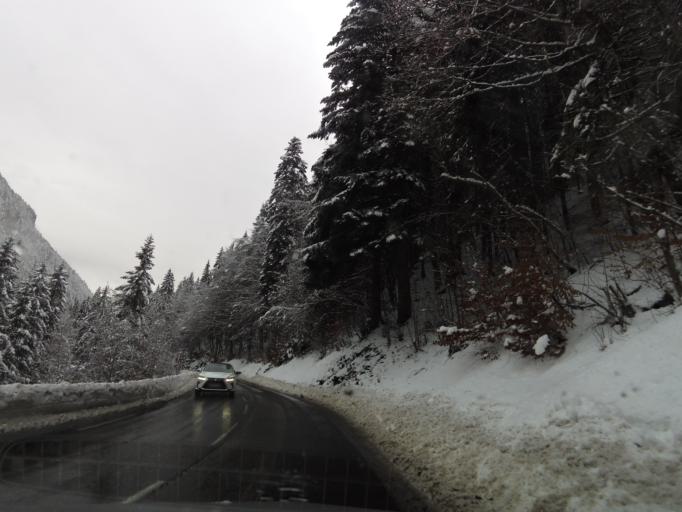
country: FR
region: Rhone-Alpes
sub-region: Departement de la Haute-Savoie
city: Les Gets
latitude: 46.1396
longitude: 6.6378
